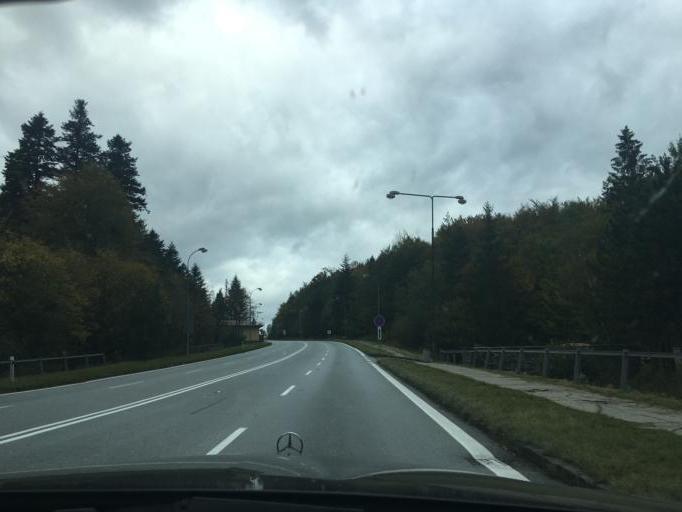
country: PL
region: Subcarpathian Voivodeship
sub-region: Powiat krosnienski
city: Jasliska
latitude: 49.4141
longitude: 21.6989
